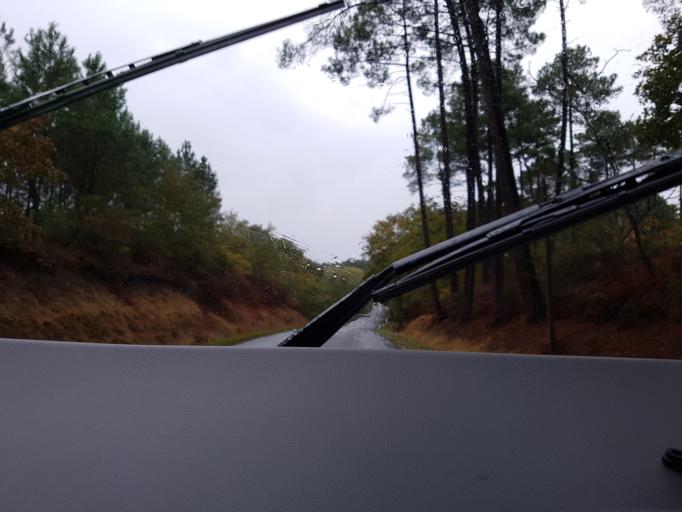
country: FR
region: Aquitaine
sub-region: Departement des Landes
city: Pissos
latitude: 44.3585
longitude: -0.6334
